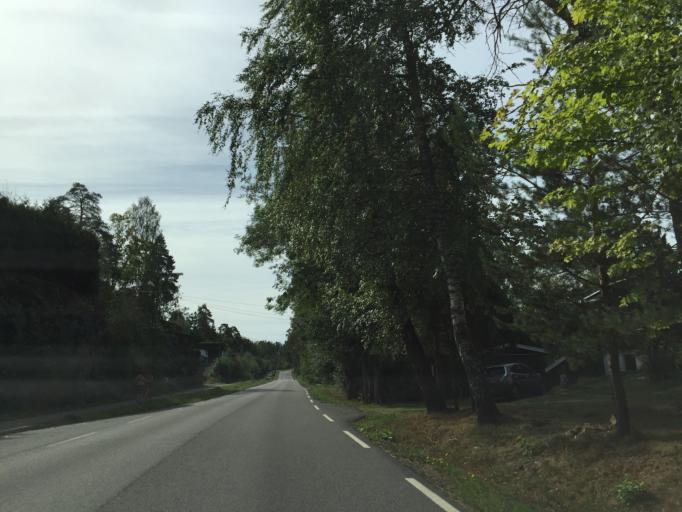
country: NO
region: Ostfold
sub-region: Moss
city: Moss
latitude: 59.5104
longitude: 10.6858
